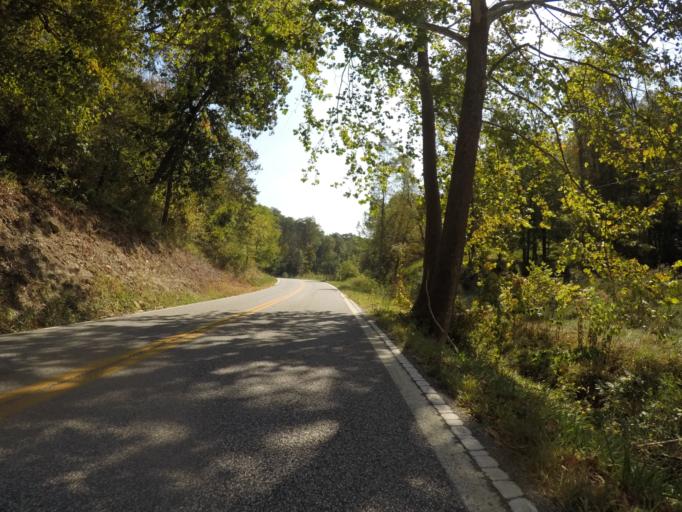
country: US
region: West Virginia
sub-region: Cabell County
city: Lesage
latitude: 38.5789
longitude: -82.4122
